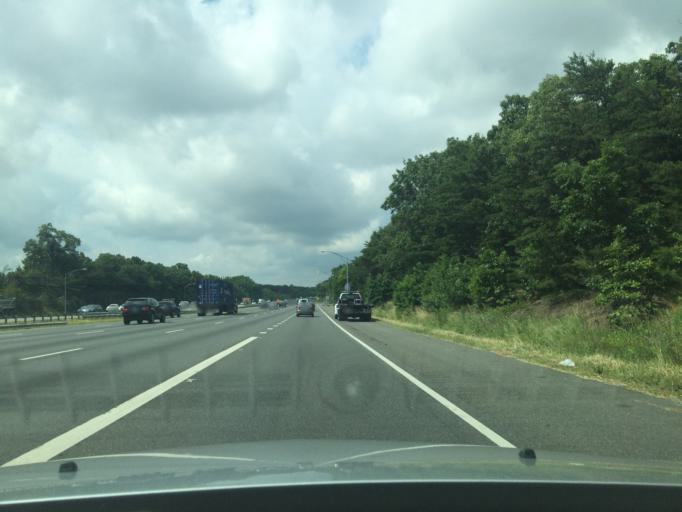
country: US
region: Maryland
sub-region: Prince George's County
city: Forestville
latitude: 38.8369
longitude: -76.8692
